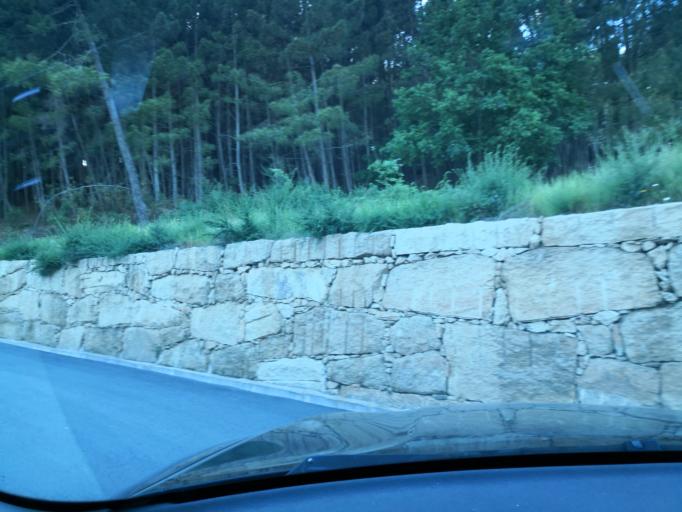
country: PT
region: Vila Real
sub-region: Vila Real
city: Vila Real
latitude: 41.3318
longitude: -7.7462
